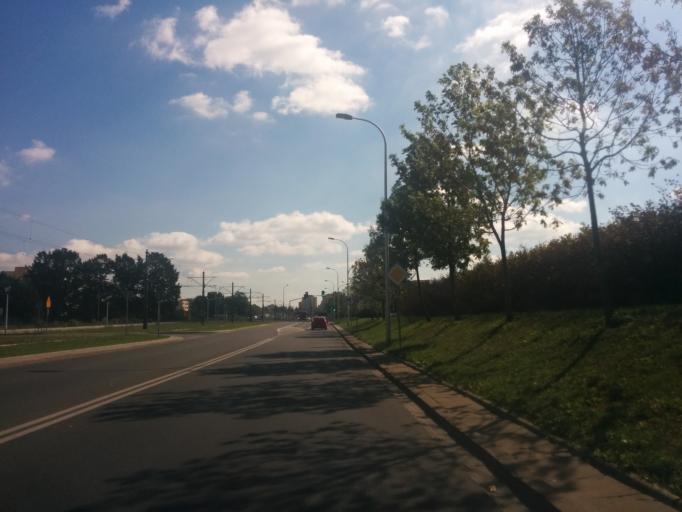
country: PL
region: Masovian Voivodeship
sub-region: Warszawa
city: Bialoleka
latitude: 52.3217
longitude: 20.9458
